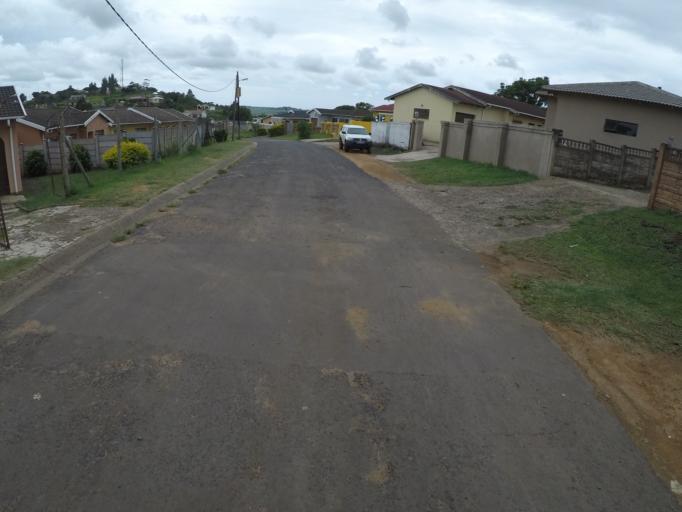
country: ZA
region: KwaZulu-Natal
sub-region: uThungulu District Municipality
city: Empangeni
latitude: -28.7847
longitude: 31.8513
